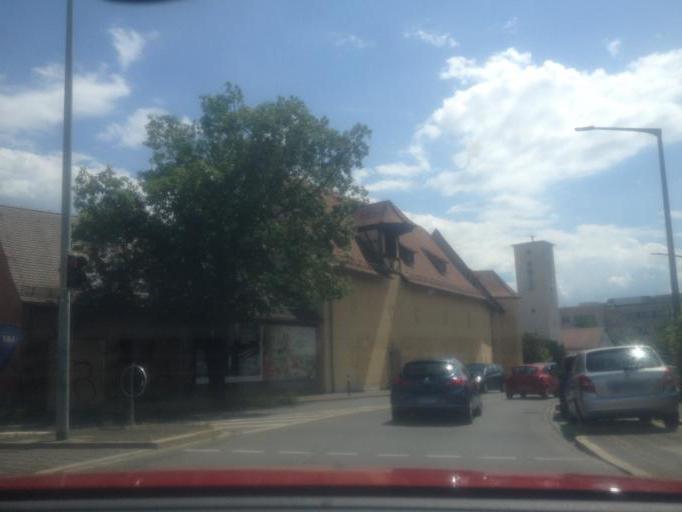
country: DE
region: Bavaria
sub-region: Regierungsbezirk Mittelfranken
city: Nuernberg
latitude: 49.4548
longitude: 11.0929
